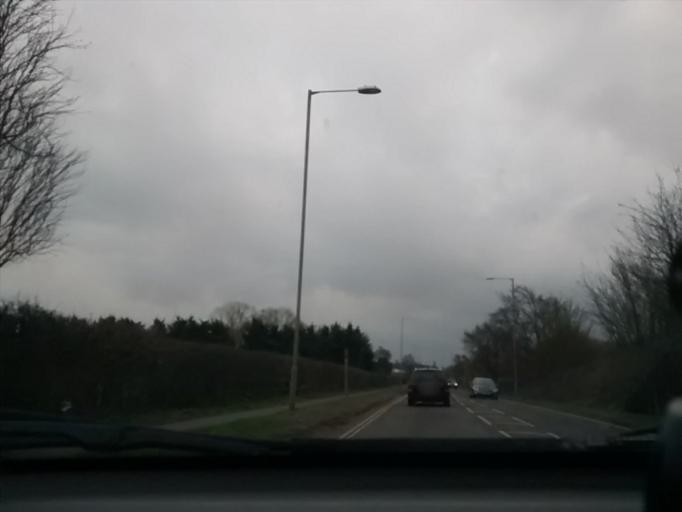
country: GB
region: England
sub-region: Cambridgeshire
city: Cambridge
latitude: 52.1711
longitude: 0.1521
